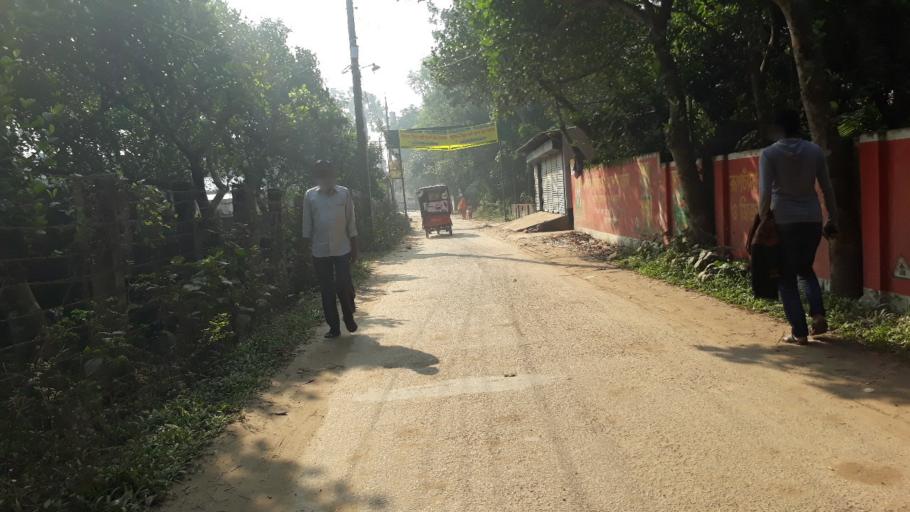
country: BD
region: Dhaka
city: Tungi
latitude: 23.8696
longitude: 90.2591
